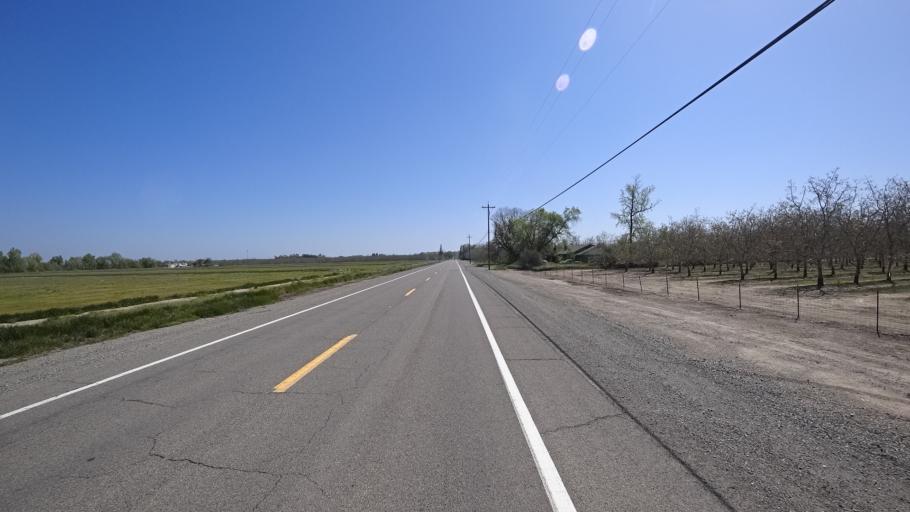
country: US
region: California
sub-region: Glenn County
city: Willows
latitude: 39.5218
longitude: -122.0247
